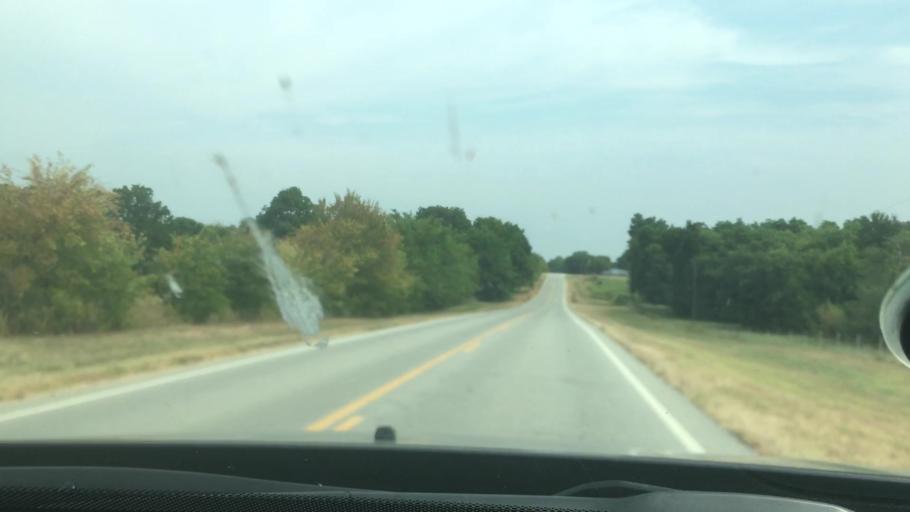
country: US
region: Oklahoma
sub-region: Coal County
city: Coalgate
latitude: 34.5256
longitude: -96.4070
